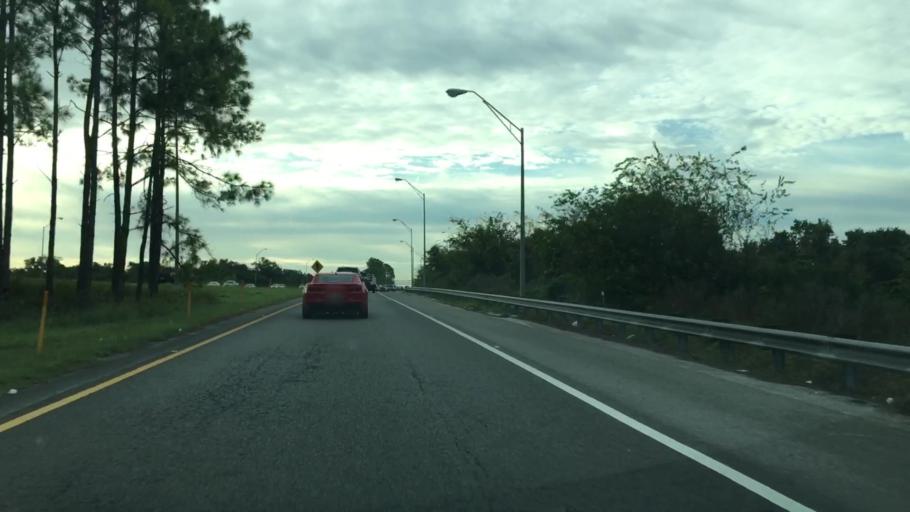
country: US
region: Florida
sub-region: Seminole County
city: Sanford
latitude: 28.7550
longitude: -81.2683
